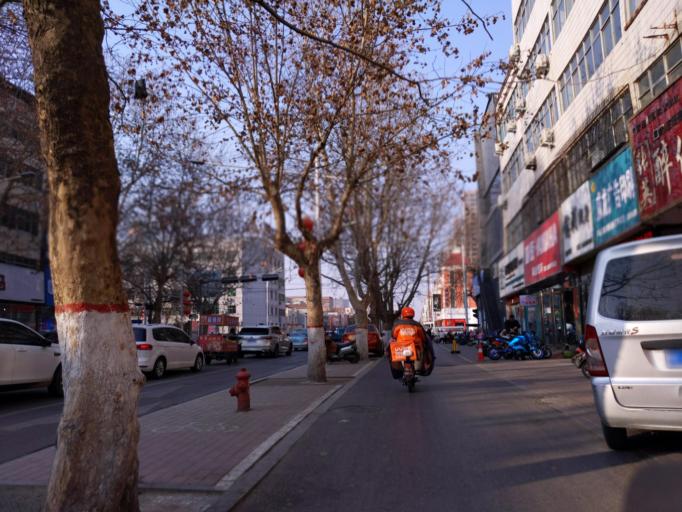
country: CN
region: Henan Sheng
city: Puyang
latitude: 35.7713
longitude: 115.0328
